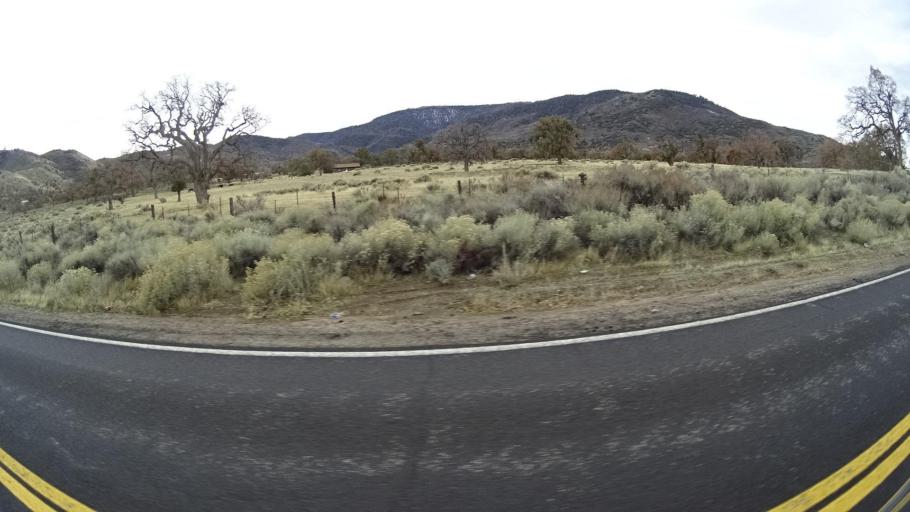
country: US
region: California
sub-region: Kern County
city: Stallion Springs
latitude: 35.0948
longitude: -118.5735
